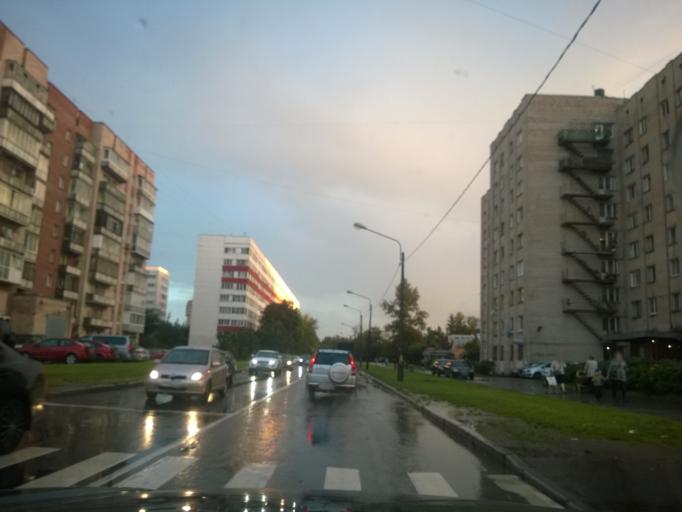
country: RU
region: St.-Petersburg
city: Uritsk
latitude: 59.8327
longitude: 30.1823
